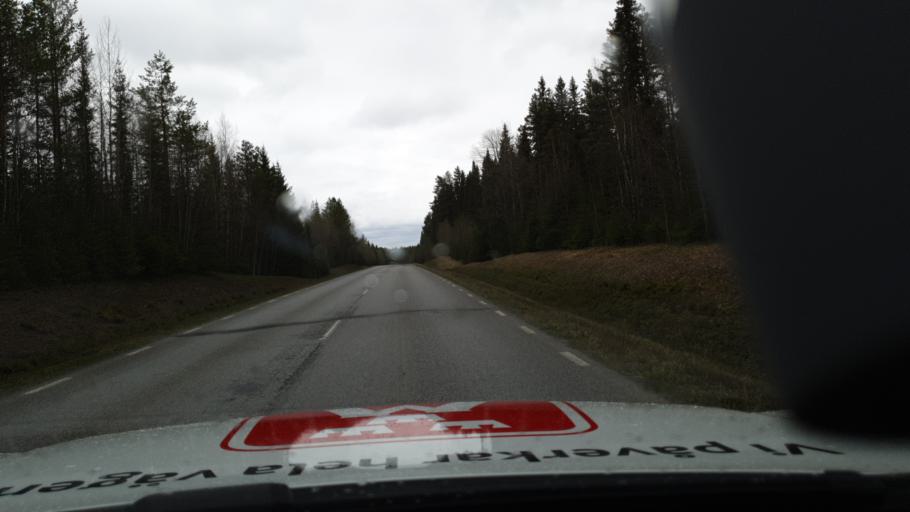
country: SE
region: Jaemtland
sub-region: Stroemsunds Kommun
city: Stroemsund
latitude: 63.6109
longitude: 15.2835
